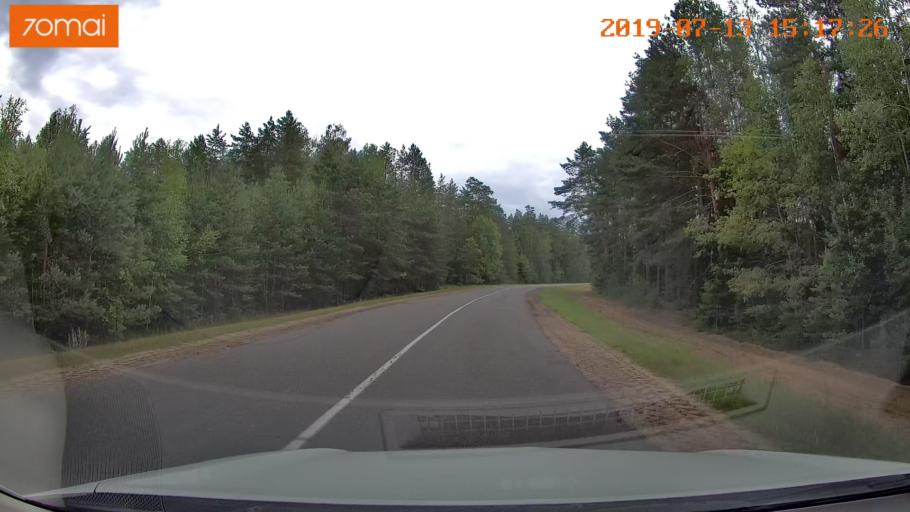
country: BY
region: Mogilev
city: Hlusha
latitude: 53.0959
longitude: 28.8445
